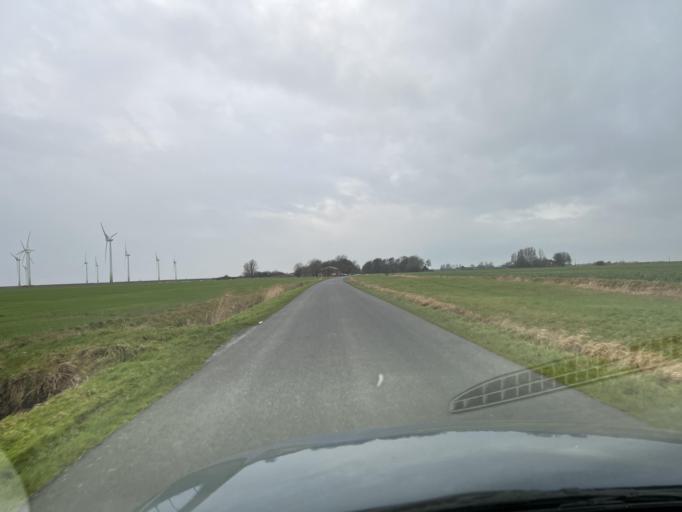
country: DE
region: Schleswig-Holstein
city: Hillgroven
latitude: 54.2159
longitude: 8.8830
